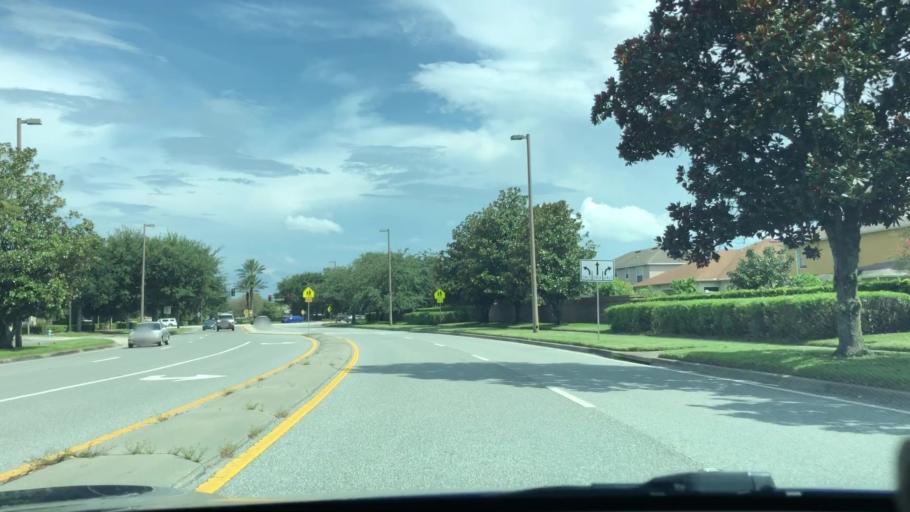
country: US
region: Florida
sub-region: Orange County
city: Conway
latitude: 28.4698
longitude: -81.2688
